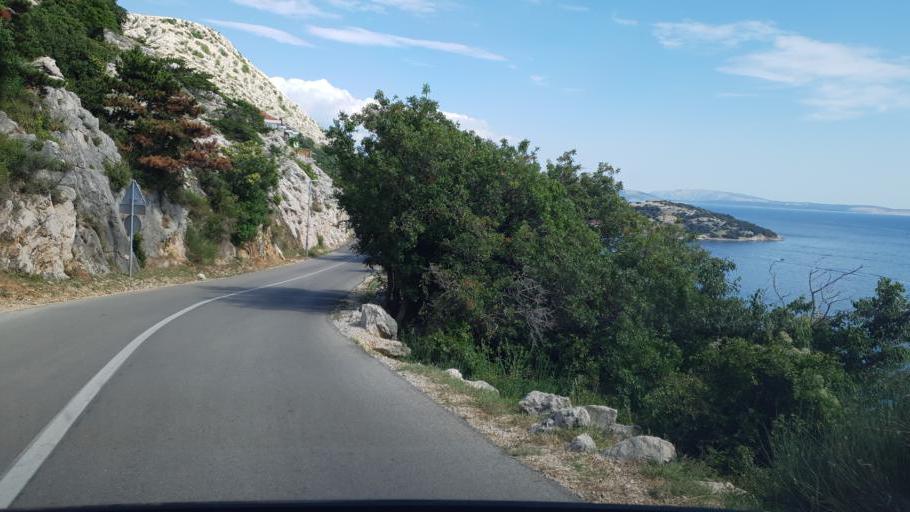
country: HR
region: Primorsko-Goranska
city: Punat
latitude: 44.9626
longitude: 14.6823
